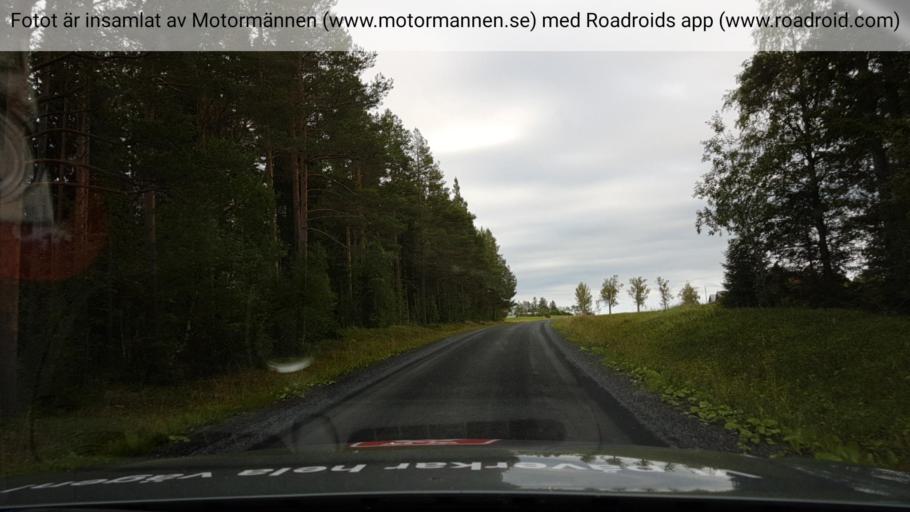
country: SE
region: Jaemtland
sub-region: Krokoms Kommun
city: Valla
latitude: 63.3660
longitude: 13.9549
